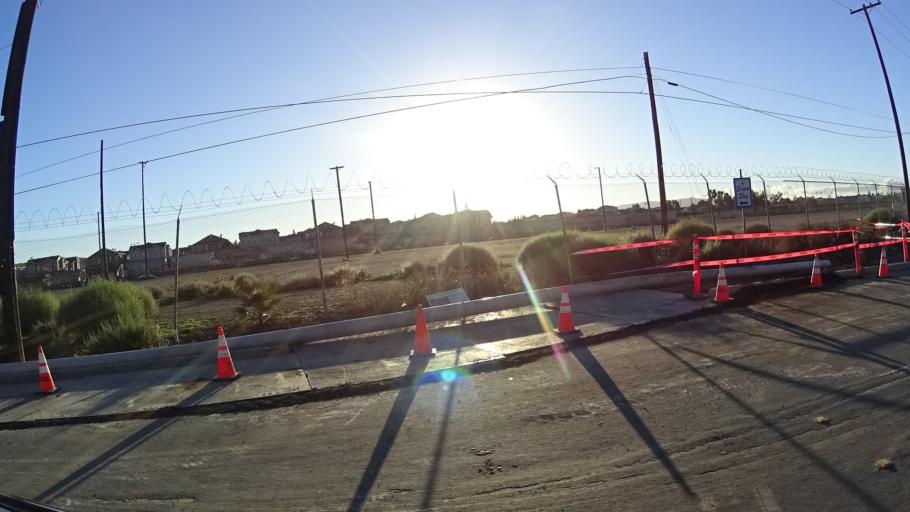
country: US
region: California
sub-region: Santa Clara County
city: Burbank
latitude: 37.3491
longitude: -121.9246
